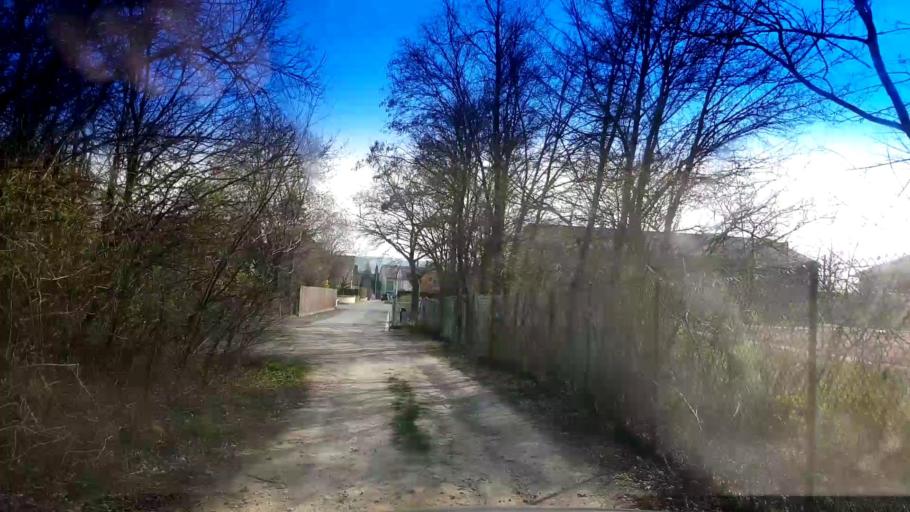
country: DE
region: Bavaria
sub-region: Upper Franconia
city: Oberhaid
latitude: 49.9374
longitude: 10.8139
